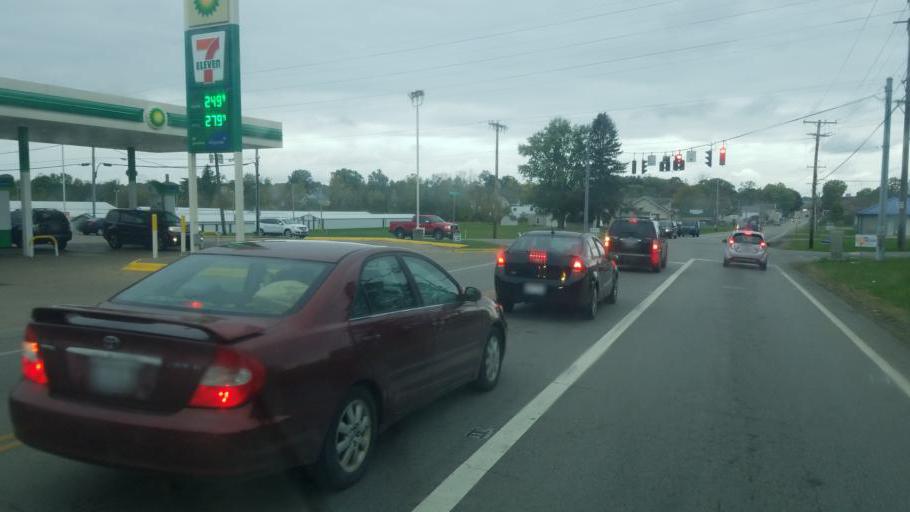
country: US
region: Ohio
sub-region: Richland County
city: Lincoln Heights
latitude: 40.7583
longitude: -82.4836
